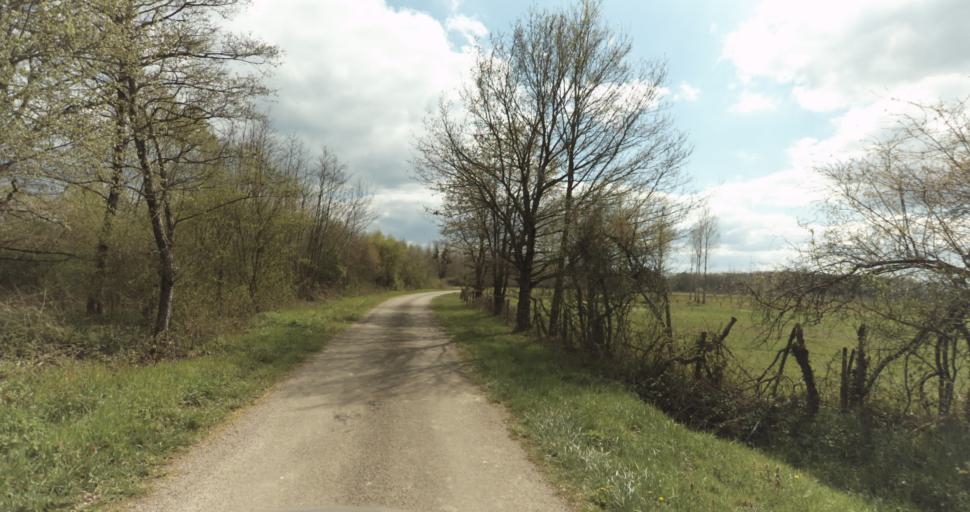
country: FR
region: Bourgogne
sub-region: Departement de la Cote-d'Or
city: Auxonne
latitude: 47.1648
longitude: 5.3957
